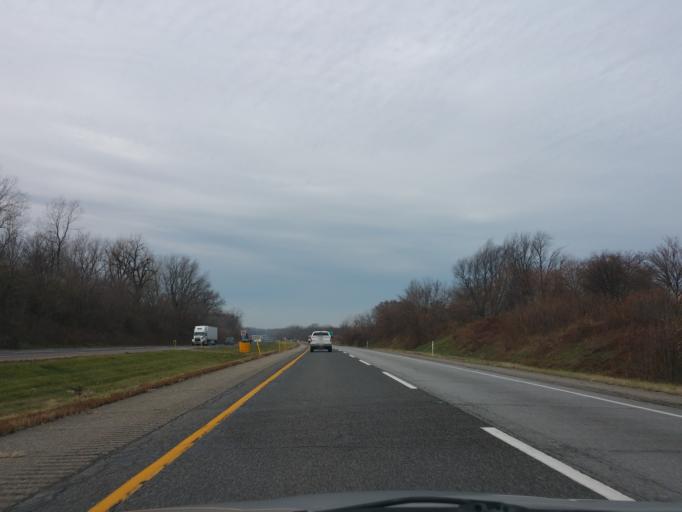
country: US
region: Indiana
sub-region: Porter County
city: Chesterton
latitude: 41.5711
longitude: -87.0011
